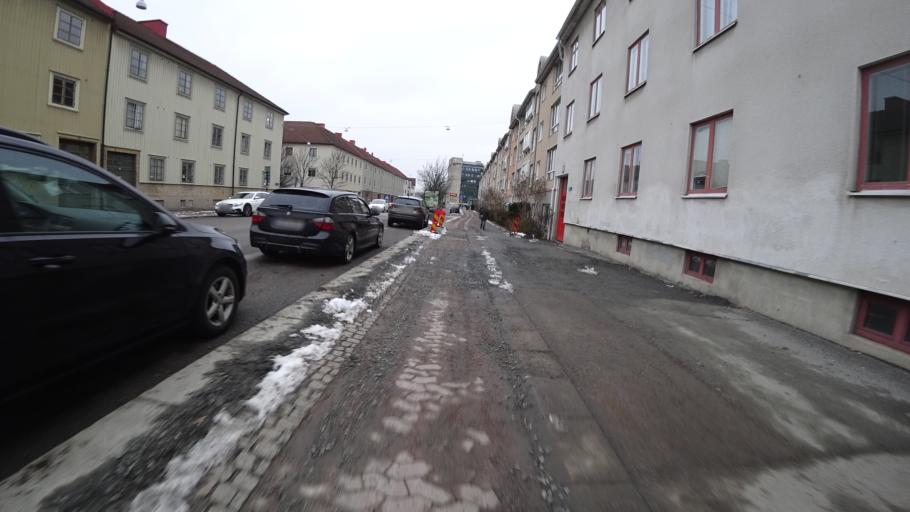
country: SE
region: Vaestra Goetaland
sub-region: Goteborg
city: Majorna
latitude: 57.6882
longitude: 11.9201
